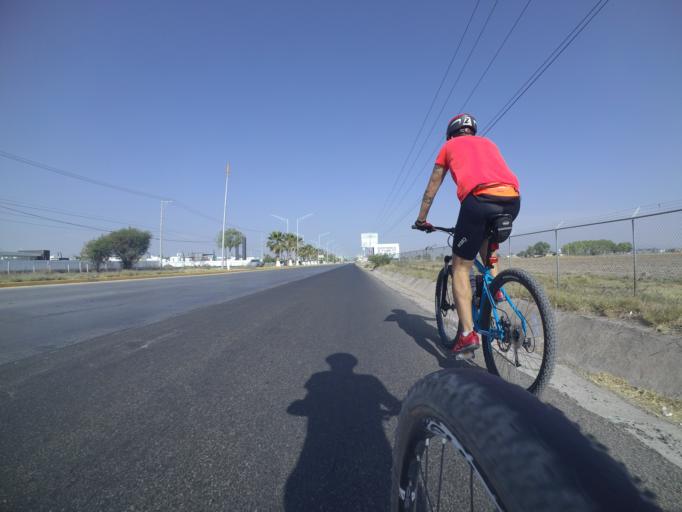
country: MX
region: Aguascalientes
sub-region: Jesus Maria
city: Arboledas Paso Blanco [Fraccionamiento]
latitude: 21.9473
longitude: -102.3046
